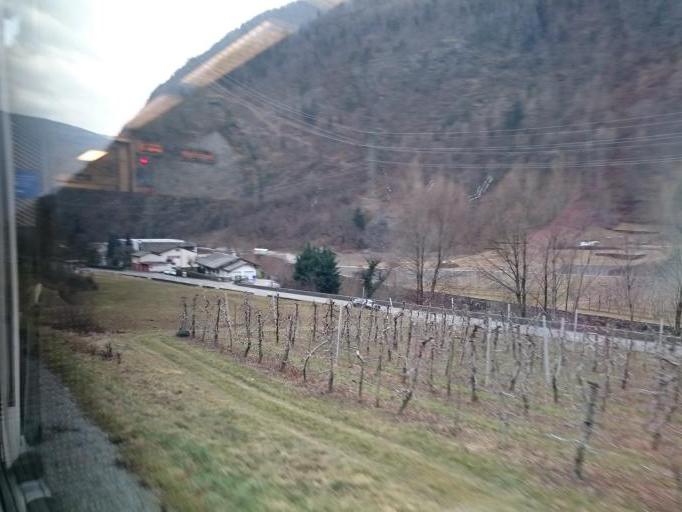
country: CH
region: Grisons
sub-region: Bernina District
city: Brusio
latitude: 46.2403
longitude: 10.1354
